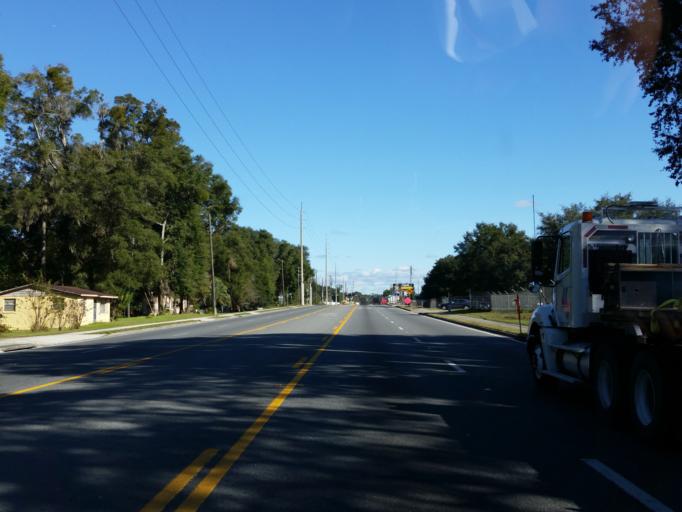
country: US
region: Florida
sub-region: Marion County
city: Ocala
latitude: 29.2669
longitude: -82.1855
